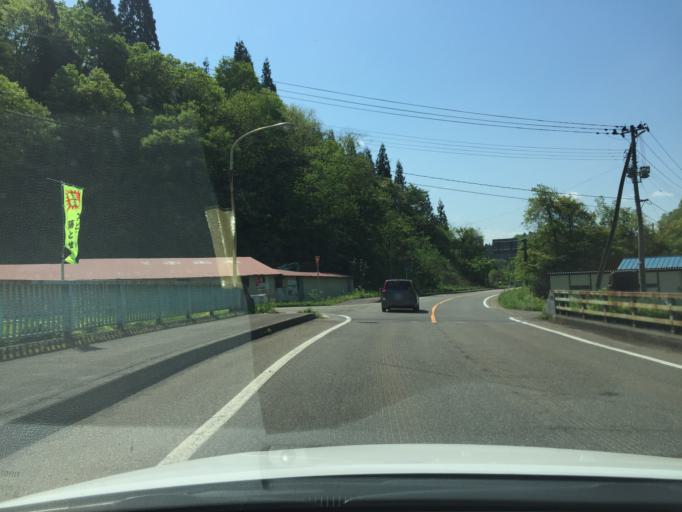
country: JP
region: Niigata
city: Kamo
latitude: 37.6255
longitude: 139.1036
